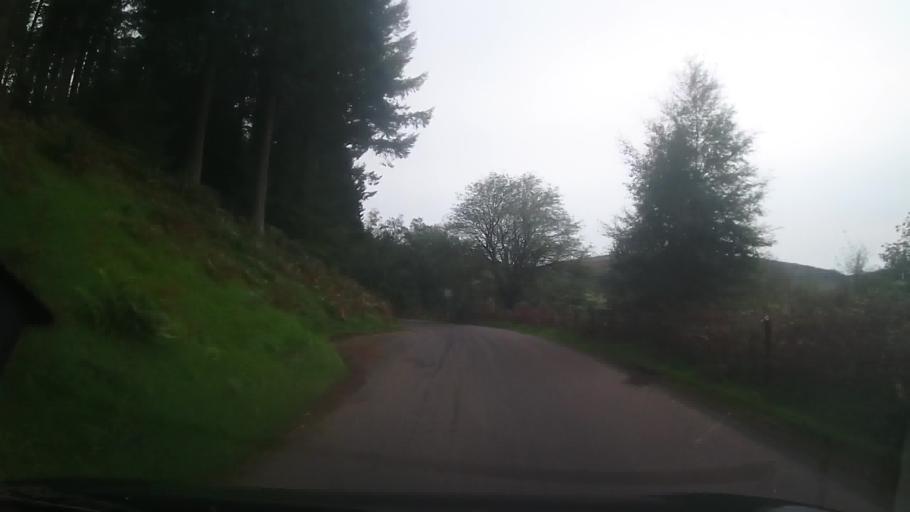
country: GB
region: Wales
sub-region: Sir Powys
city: Rhayader
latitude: 52.2929
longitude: -3.6049
